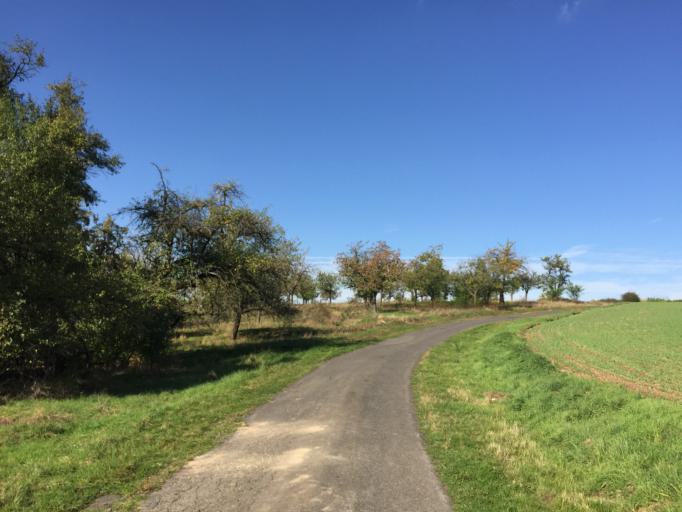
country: DE
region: Hesse
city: Lollar
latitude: 50.6220
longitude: 8.6944
